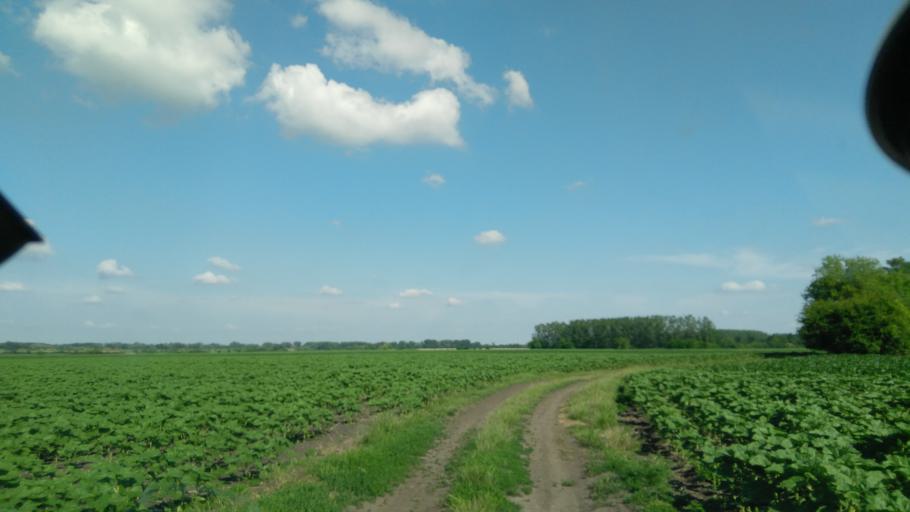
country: HU
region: Bekes
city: Doboz
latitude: 46.7035
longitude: 21.2332
